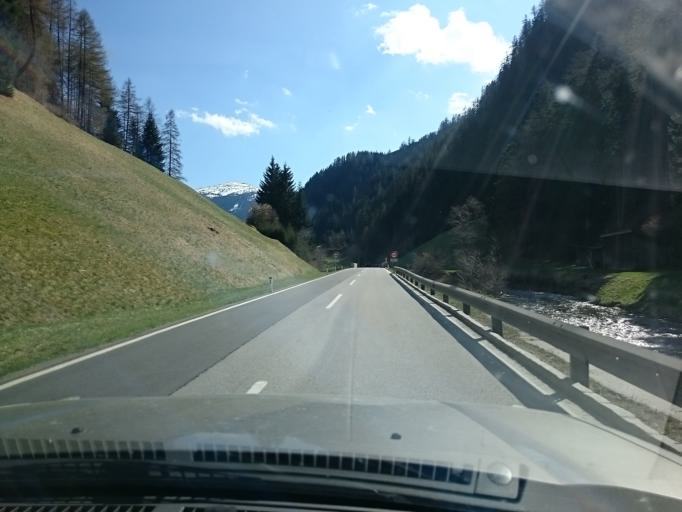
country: AT
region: Tyrol
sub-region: Politischer Bezirk Innsbruck Land
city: Gries am Brenner
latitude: 47.0615
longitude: 11.4863
